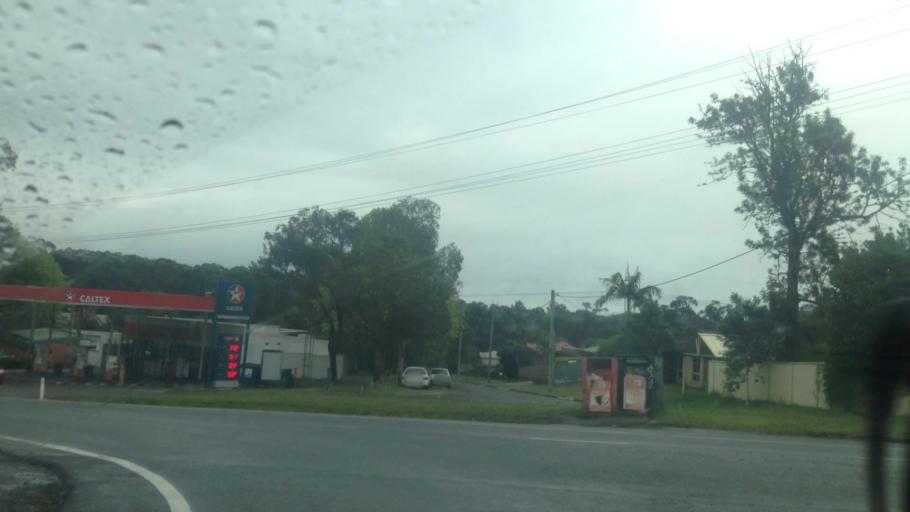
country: AU
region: New South Wales
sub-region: Wyong Shire
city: Charmhaven
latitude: -33.1759
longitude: 151.4810
